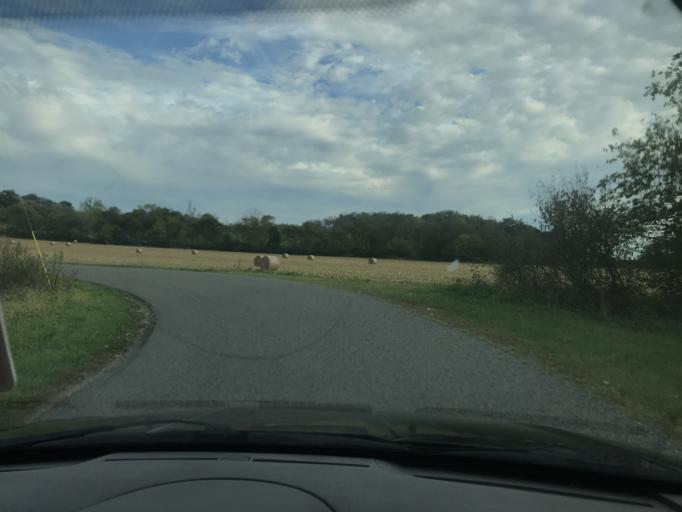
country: US
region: Ohio
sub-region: Logan County
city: West Liberty
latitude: 40.2480
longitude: -83.6944
